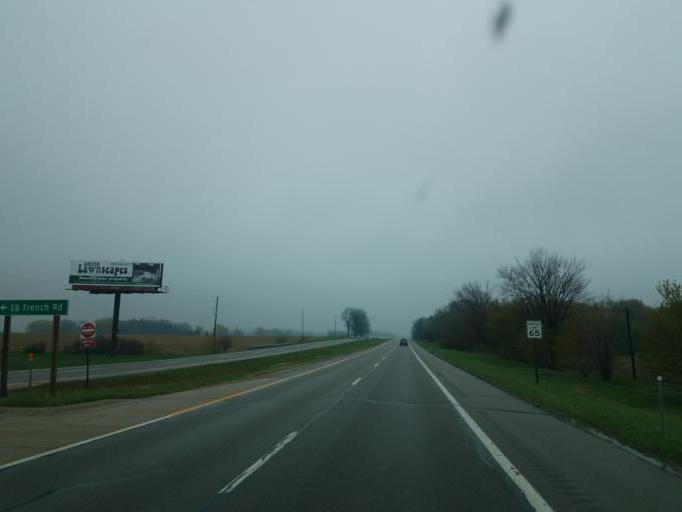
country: US
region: Michigan
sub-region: Clinton County
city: Saint Johns
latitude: 43.0582
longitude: -84.5639
